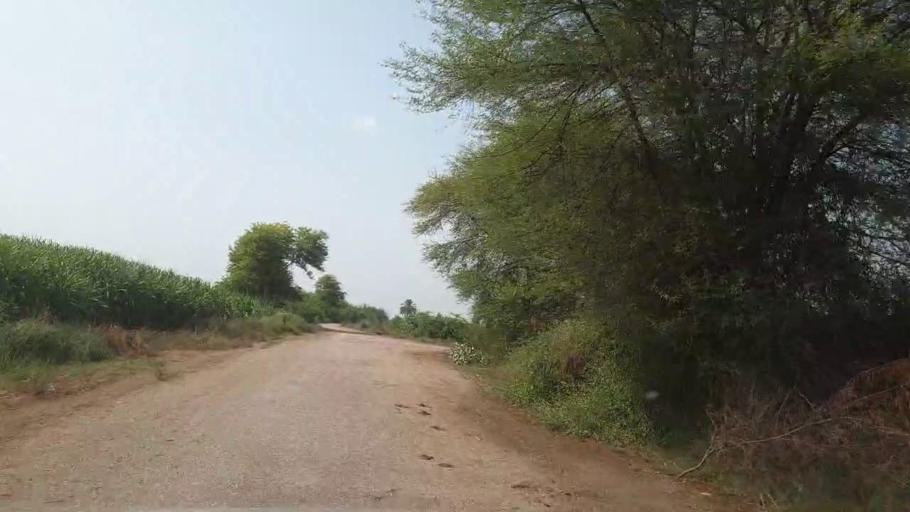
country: PK
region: Sindh
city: Pano Aqil
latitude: 27.7782
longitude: 69.1610
